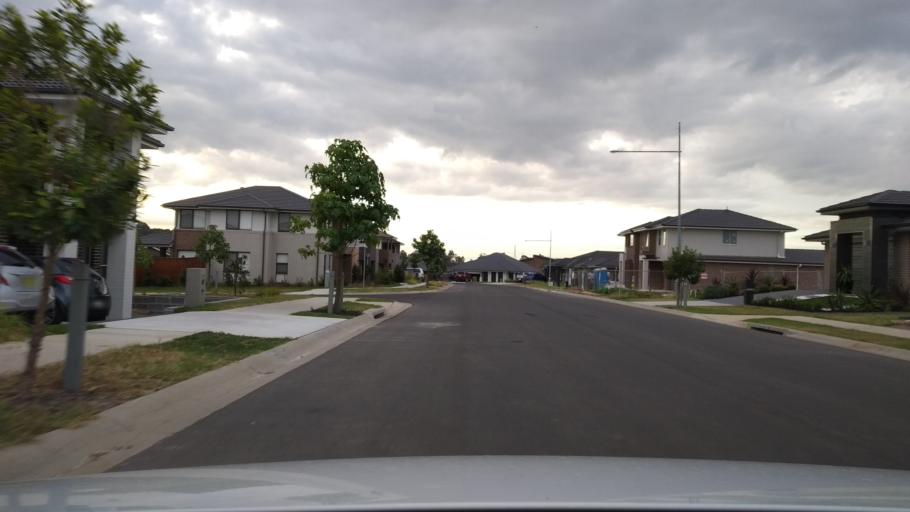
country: AU
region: New South Wales
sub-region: Camden
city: Narellan
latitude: -34.0003
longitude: 150.7307
